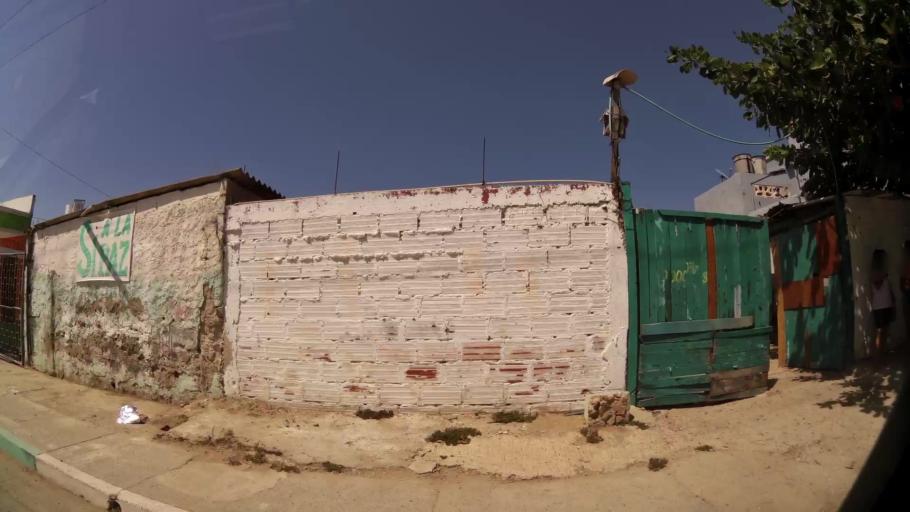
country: CO
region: Bolivar
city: Cartagena
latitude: 10.4356
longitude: -75.5300
